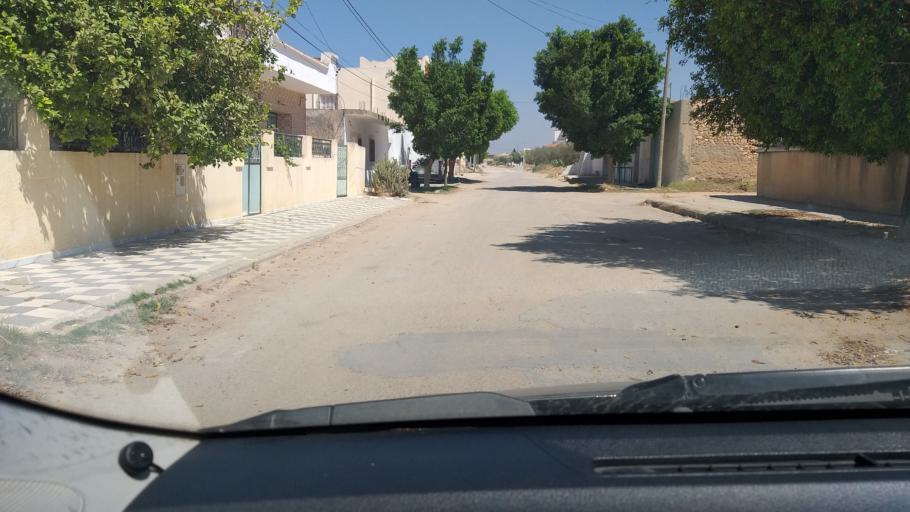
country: TN
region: Al Mahdiyah
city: El Jem
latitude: 35.2906
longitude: 10.7176
